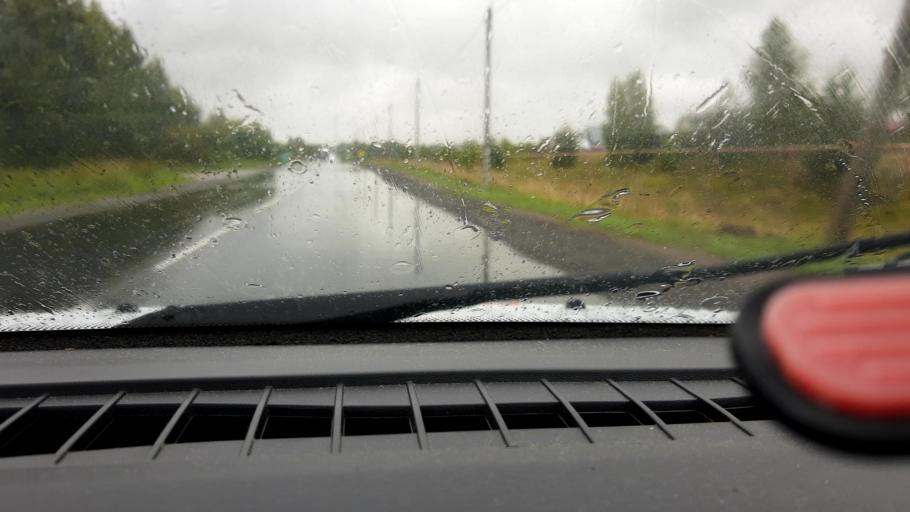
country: RU
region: Nizjnij Novgorod
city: Lyskovo
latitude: 56.0279
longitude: 45.0159
